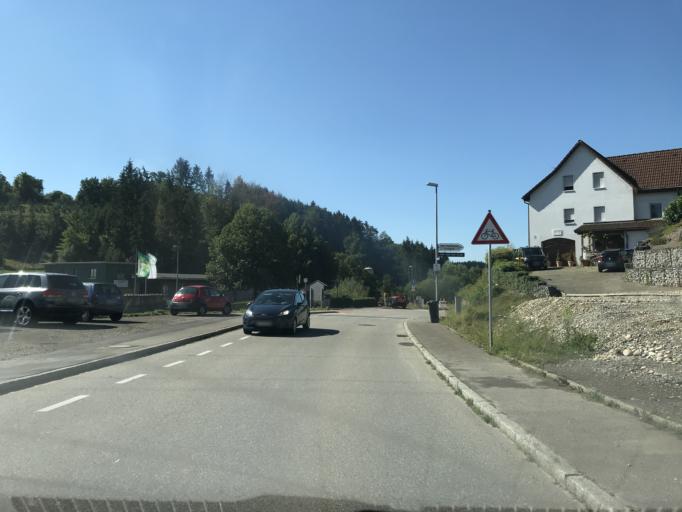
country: DE
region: Baden-Wuerttemberg
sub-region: Freiburg Region
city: Rheinfelden (Baden)
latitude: 47.5926
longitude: 7.7913
